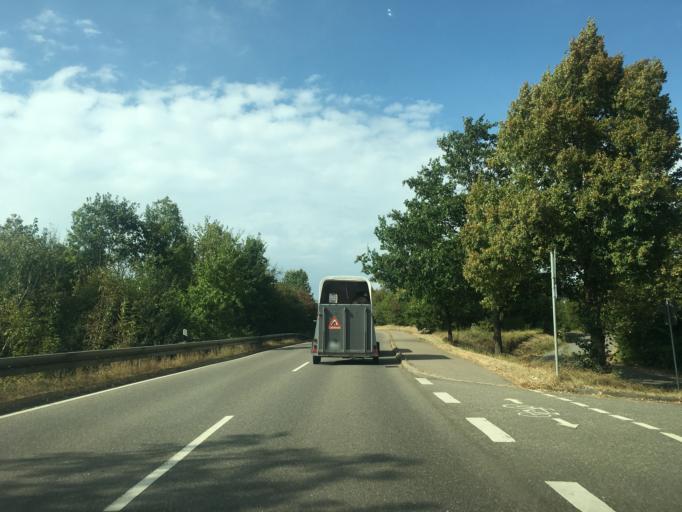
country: DE
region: Baden-Wuerttemberg
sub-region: Tuebingen Region
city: Wannweil
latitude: 48.4731
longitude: 9.1538
